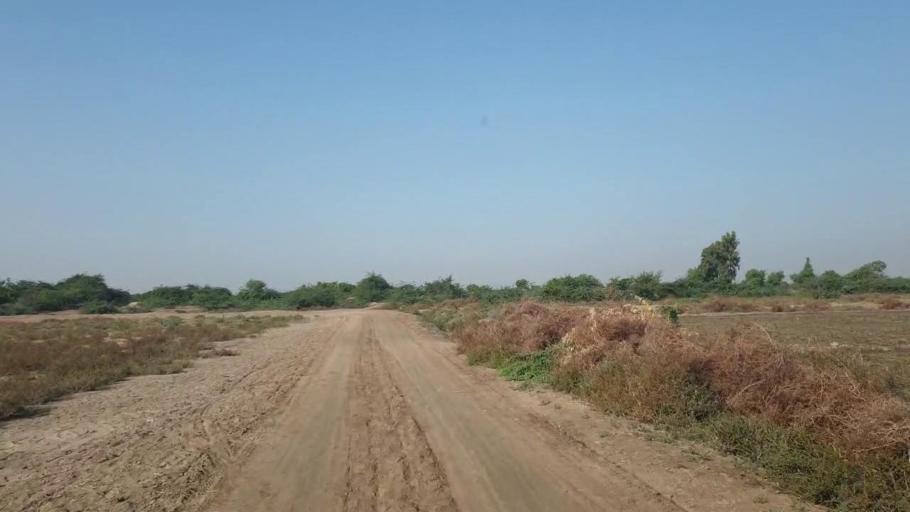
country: PK
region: Sindh
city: Badin
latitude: 24.4537
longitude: 68.7239
